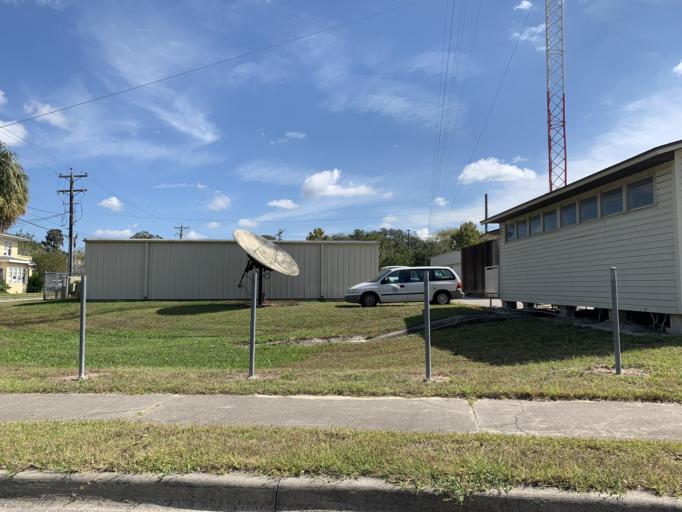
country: US
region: Florida
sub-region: Marion County
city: Ocala
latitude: 29.1831
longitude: -82.1335
